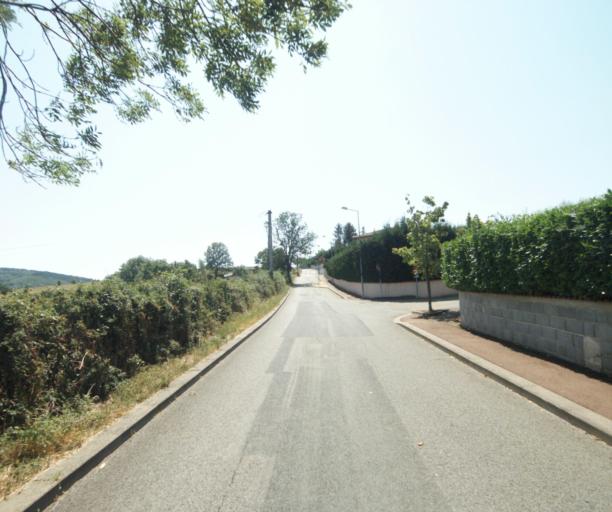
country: FR
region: Rhone-Alpes
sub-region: Departement du Rhone
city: Saint-Pierre-la-Palud
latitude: 45.7945
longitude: 4.6139
